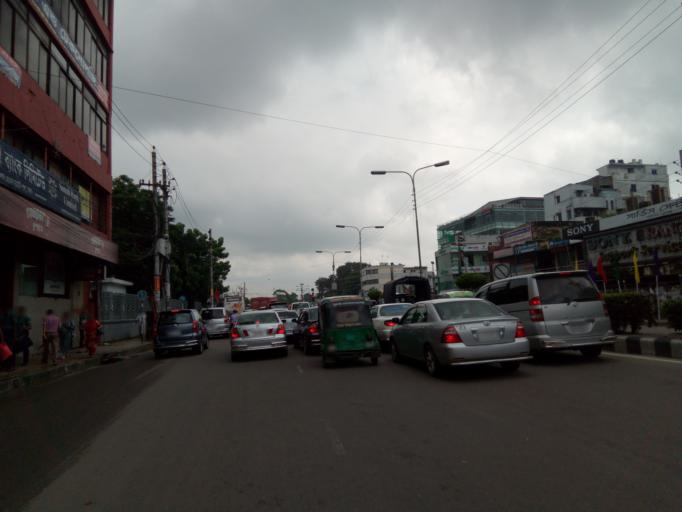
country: BD
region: Dhaka
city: Azimpur
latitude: 23.7635
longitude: 90.3891
